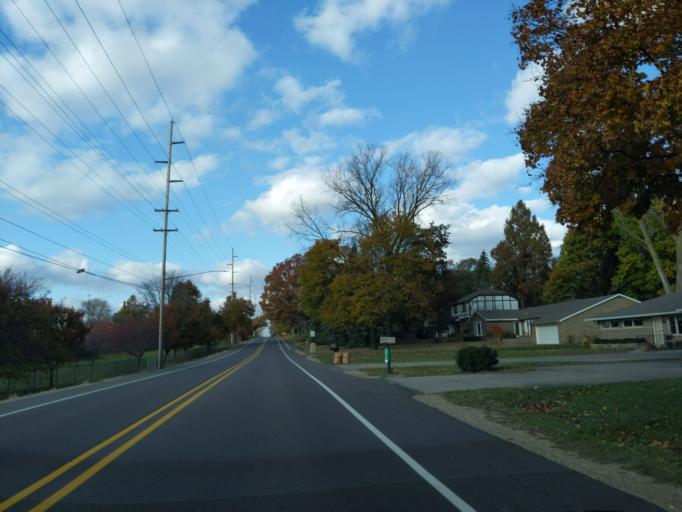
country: US
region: Michigan
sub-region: Ingham County
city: Lansing
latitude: 42.7492
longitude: -84.5231
